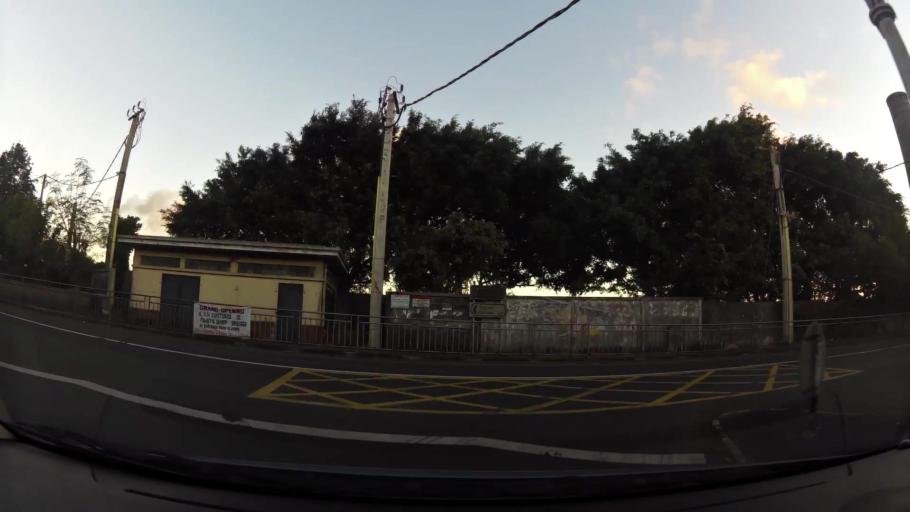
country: MU
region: Moka
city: Verdun
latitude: -20.2242
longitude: 57.5352
